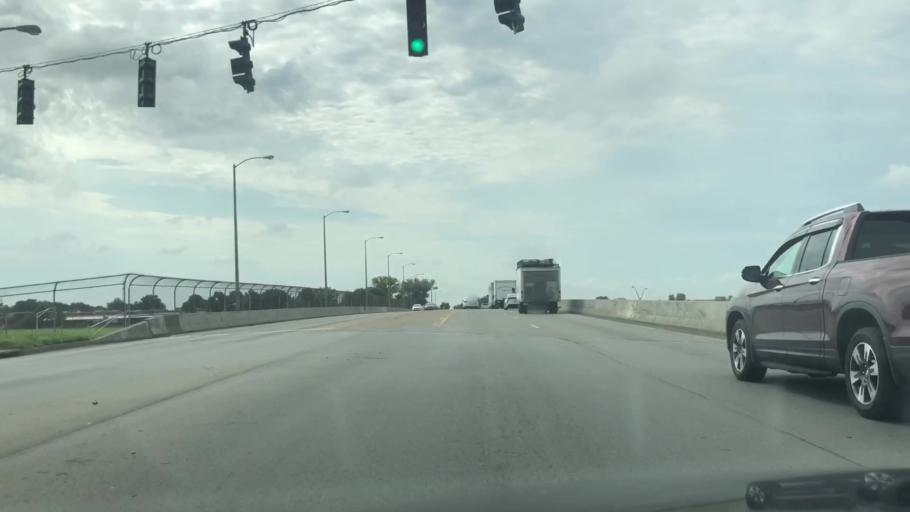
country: US
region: Kentucky
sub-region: Jefferson County
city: Audubon Park
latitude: 38.1915
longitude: -85.7277
